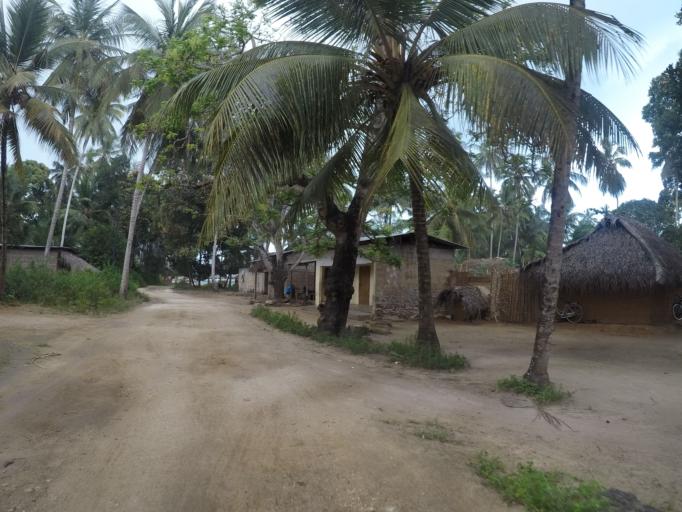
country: TZ
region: Zanzibar North
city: Mkokotoni
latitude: -5.9544
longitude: 39.1940
